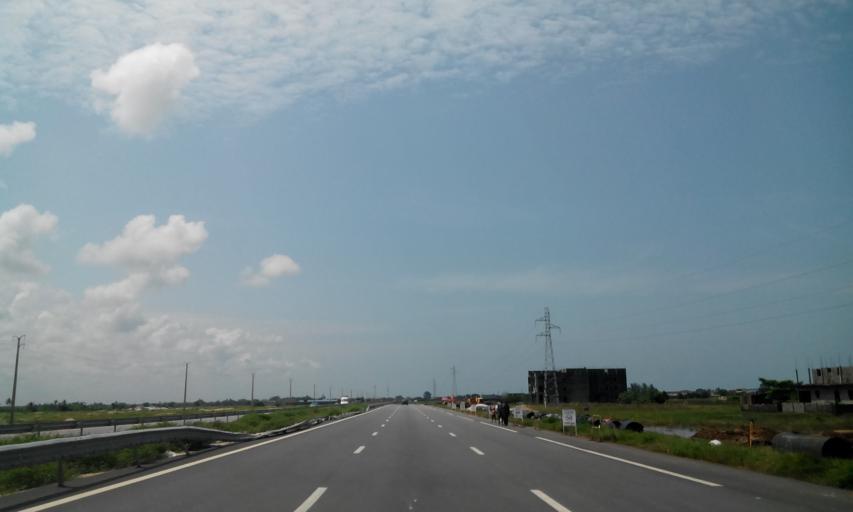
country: CI
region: Sud-Comoe
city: Grand-Bassam
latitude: 5.2290
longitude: -3.7489
